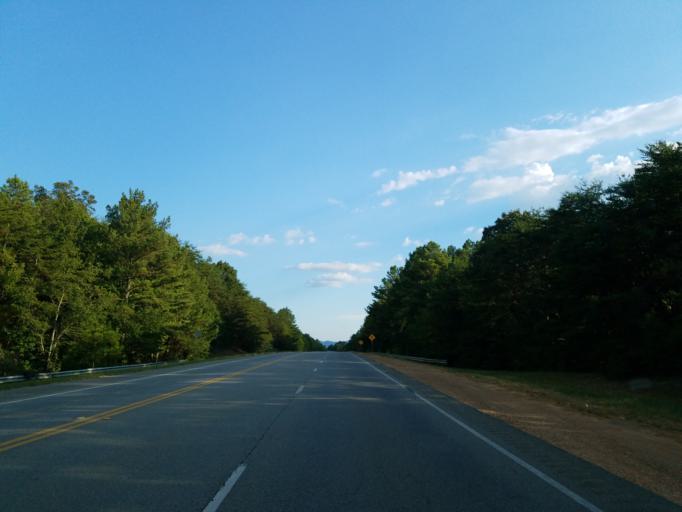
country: US
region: Georgia
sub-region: Murray County
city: Chatsworth
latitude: 34.6840
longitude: -84.7293
